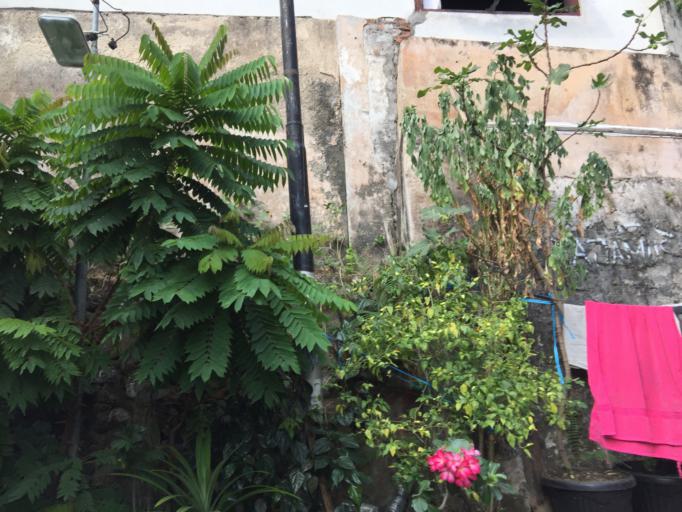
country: ID
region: Daerah Istimewa Yogyakarta
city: Yogyakarta
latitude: -7.7941
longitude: 110.3701
